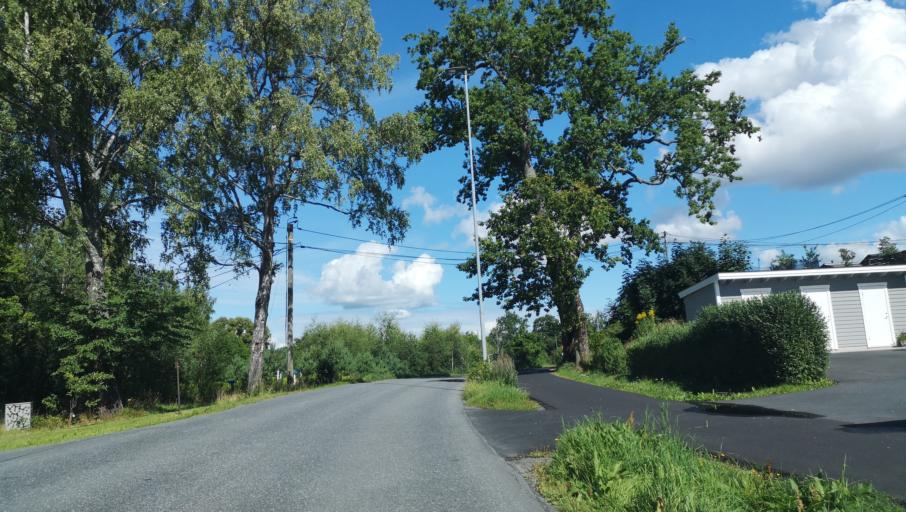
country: NO
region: Akershus
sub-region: Frogn
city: Drobak
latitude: 59.6603
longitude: 10.6394
